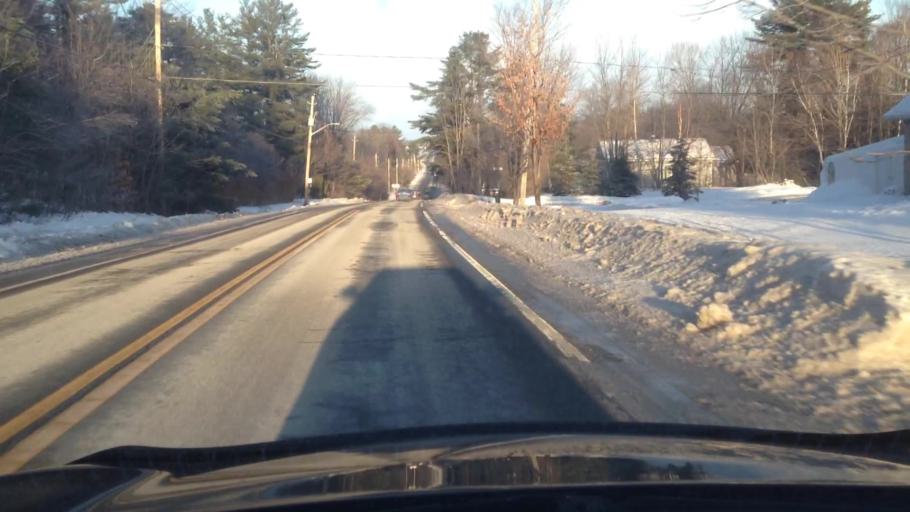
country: CA
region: Quebec
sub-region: Lanaudiere
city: Sainte-Julienne
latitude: 45.9339
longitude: -73.7387
